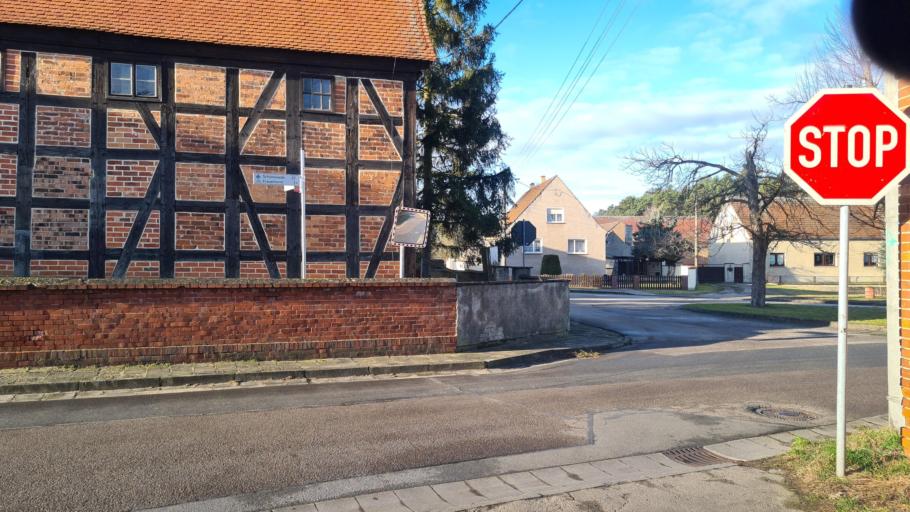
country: DE
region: Brandenburg
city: Herzberg
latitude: 51.6969
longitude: 13.1756
